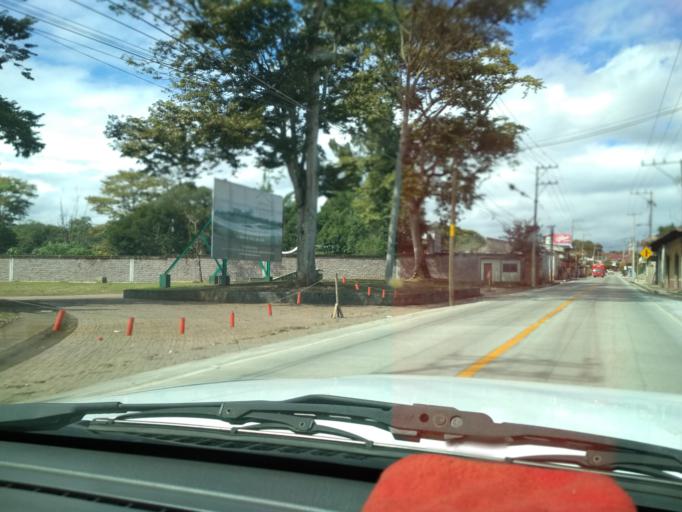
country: MX
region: Veracruz
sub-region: Coatepec
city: Las Lomas
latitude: 19.4349
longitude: -96.9182
